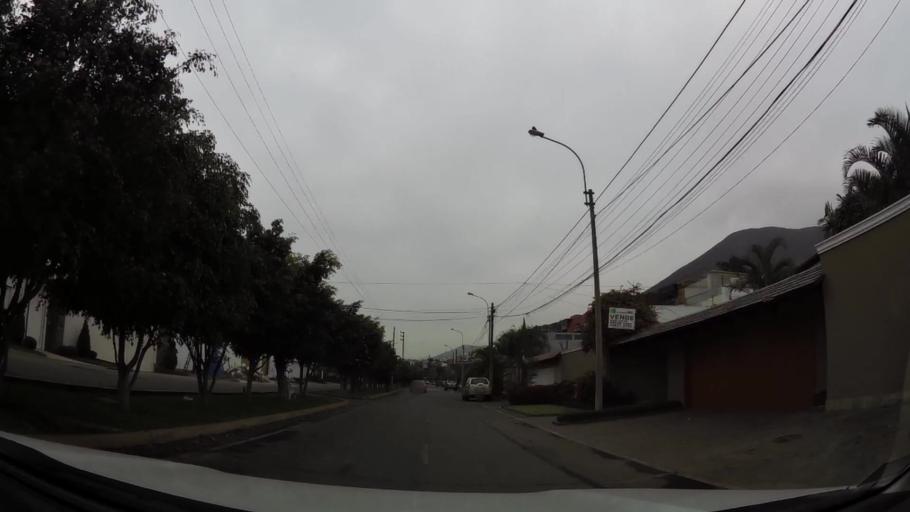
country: PE
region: Lima
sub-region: Lima
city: La Molina
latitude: -12.0841
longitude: -76.9219
